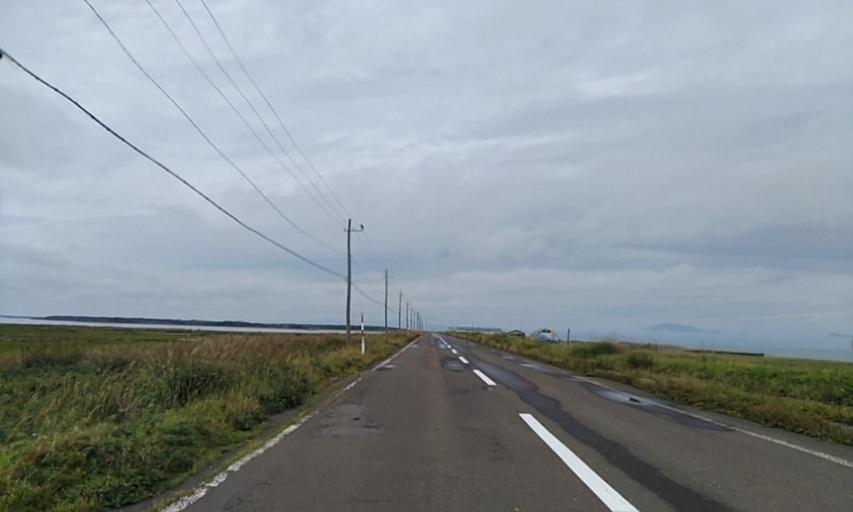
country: JP
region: Hokkaido
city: Shibetsu
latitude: 43.5971
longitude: 145.3212
